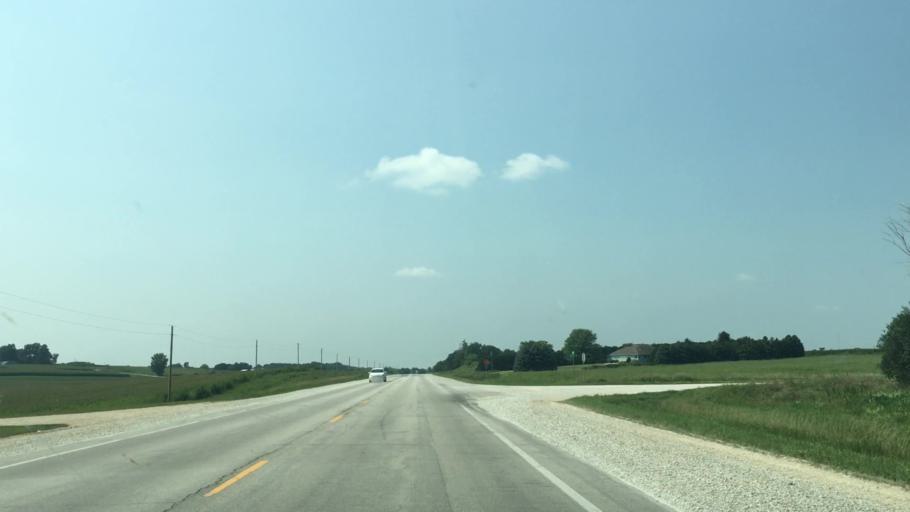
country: US
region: Iowa
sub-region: Winneshiek County
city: Decorah
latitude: 43.3971
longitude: -91.8390
